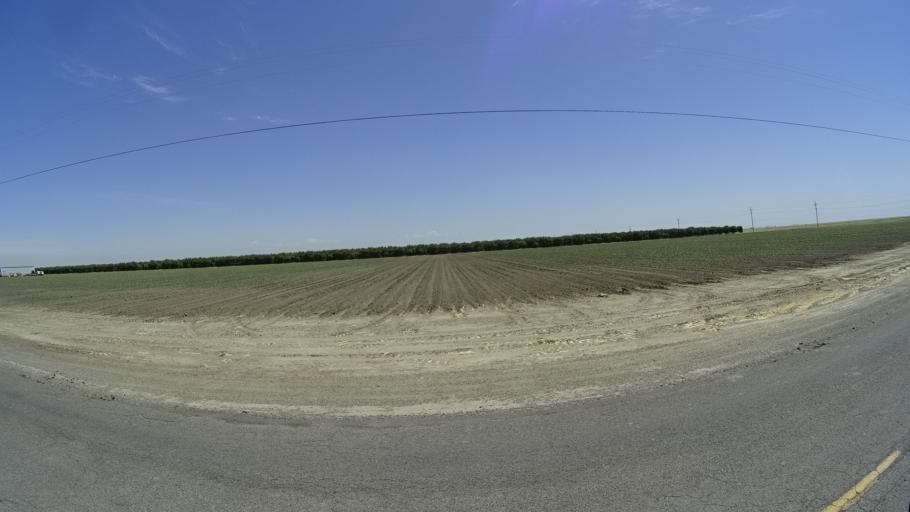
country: US
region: California
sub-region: Kings County
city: Corcoran
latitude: 36.1107
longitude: -119.6258
